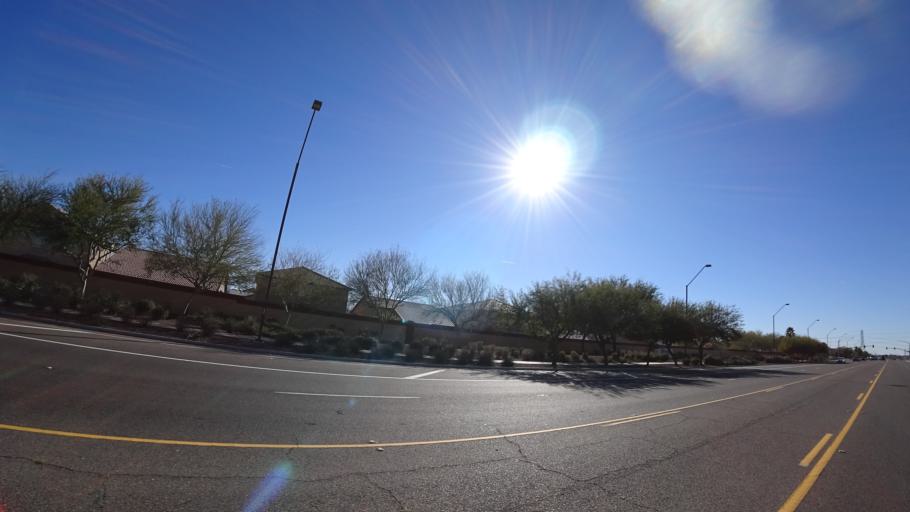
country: US
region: Arizona
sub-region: Maricopa County
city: Avondale
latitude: 33.4354
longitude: -112.3121
